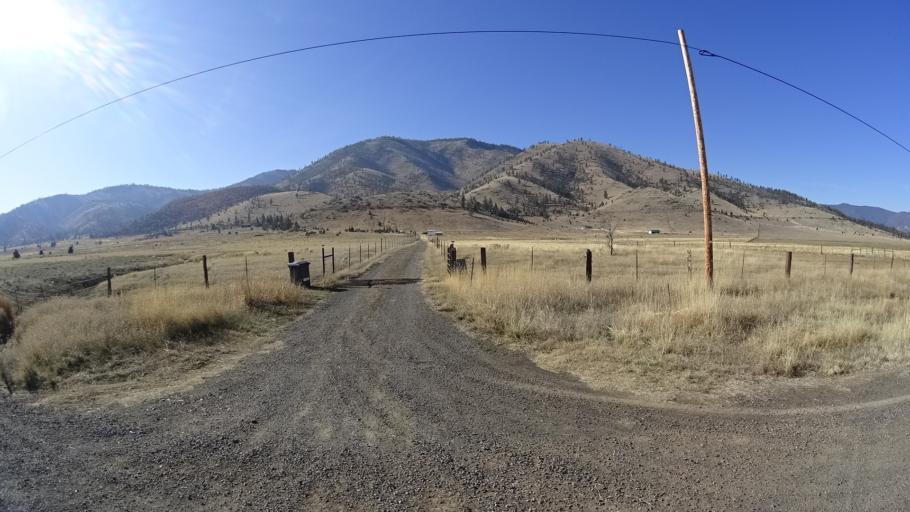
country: US
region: California
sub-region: Siskiyou County
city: Weed
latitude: 41.4830
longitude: -122.4953
